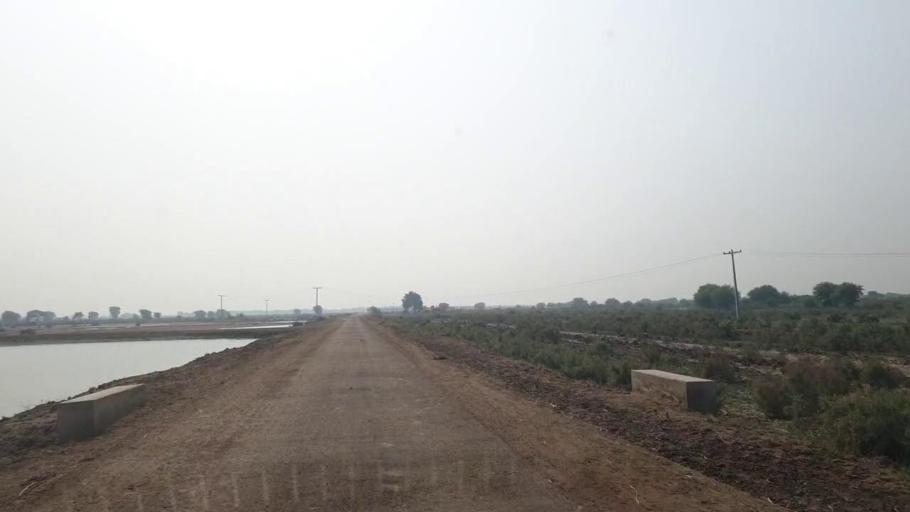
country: PK
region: Sindh
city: Matli
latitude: 25.1406
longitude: 68.6906
